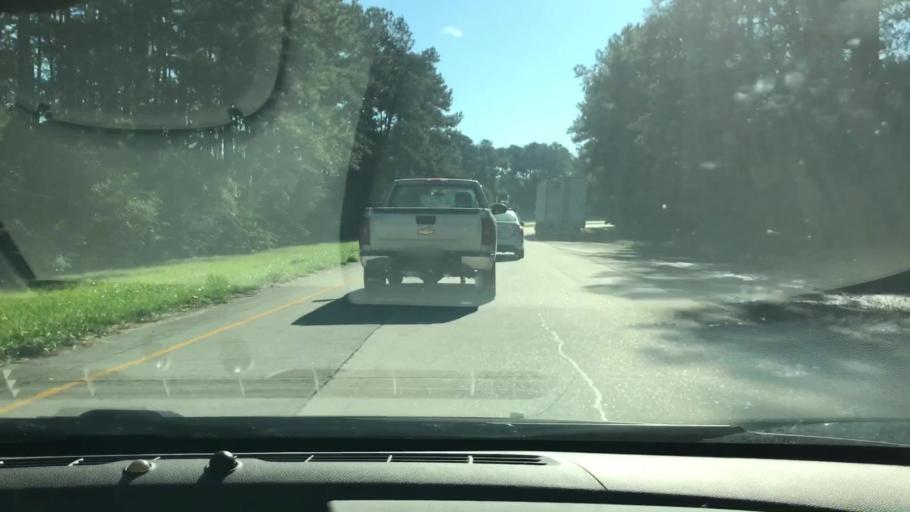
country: US
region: Louisiana
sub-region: Saint Tammany Parish
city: Pearl River
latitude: 30.3535
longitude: -89.7420
